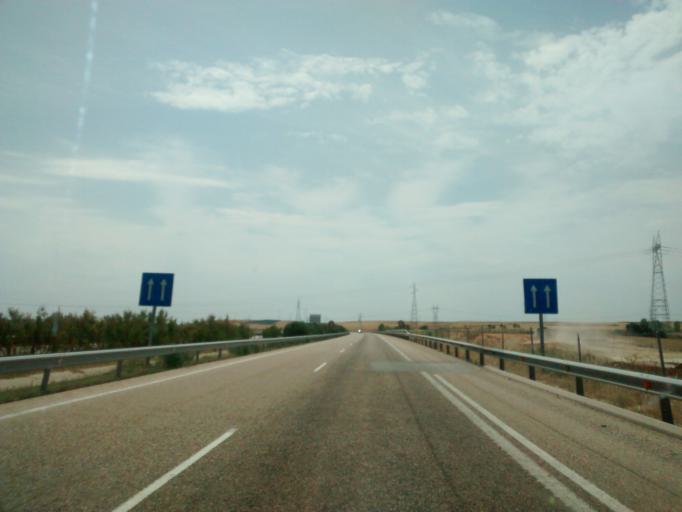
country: ES
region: Castille and Leon
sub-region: Provincia de Burgos
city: San Mames de Burgos
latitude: 42.3427
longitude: -3.7903
